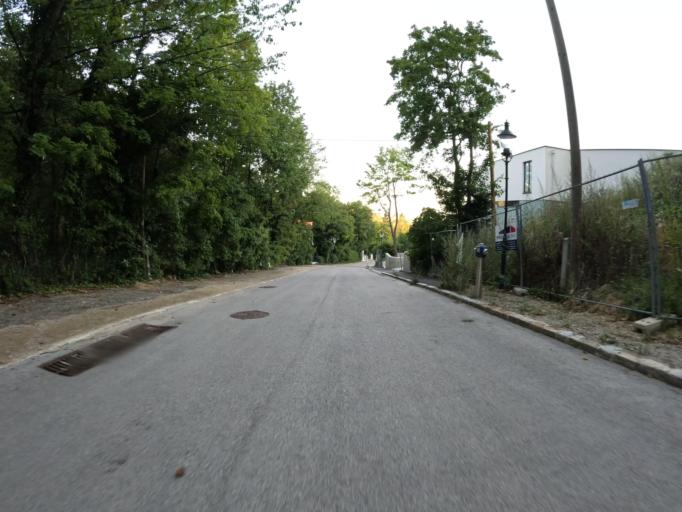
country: AT
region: Lower Austria
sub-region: Politischer Bezirk Baden
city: Baden
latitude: 48.0168
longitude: 16.2241
